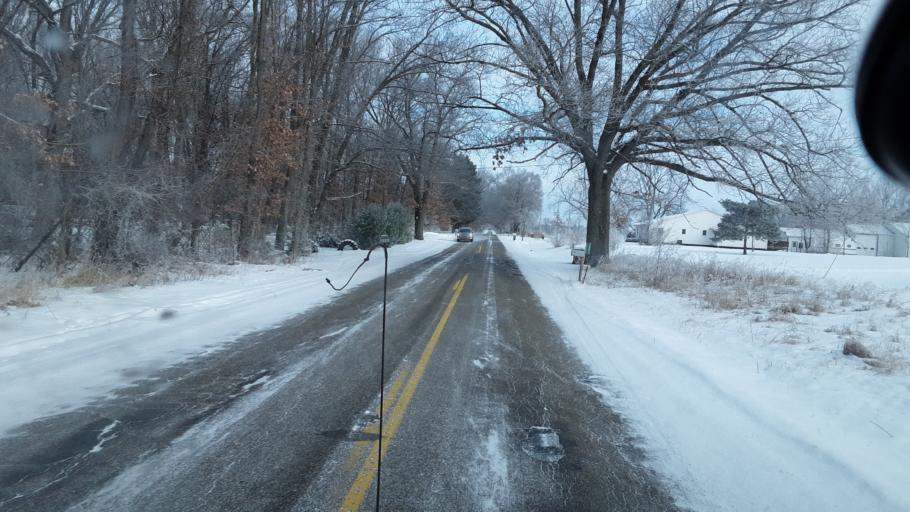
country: US
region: Michigan
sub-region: Ingham County
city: Leslie
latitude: 42.3772
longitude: -84.4924
